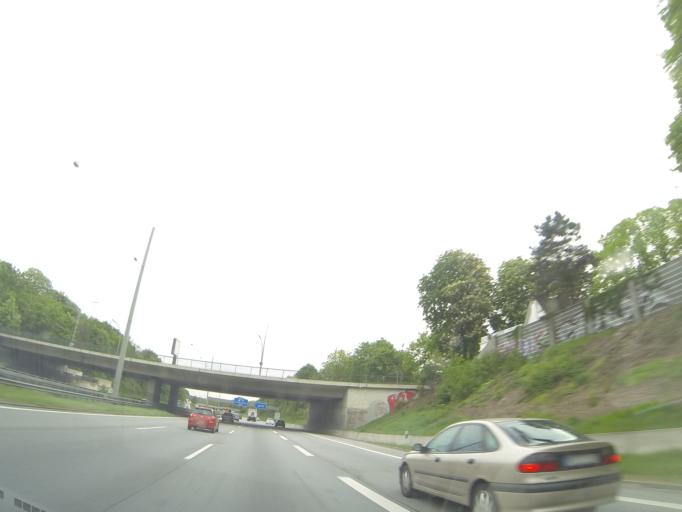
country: DE
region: Hamburg
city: Stellingen
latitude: 53.5707
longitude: 9.9022
